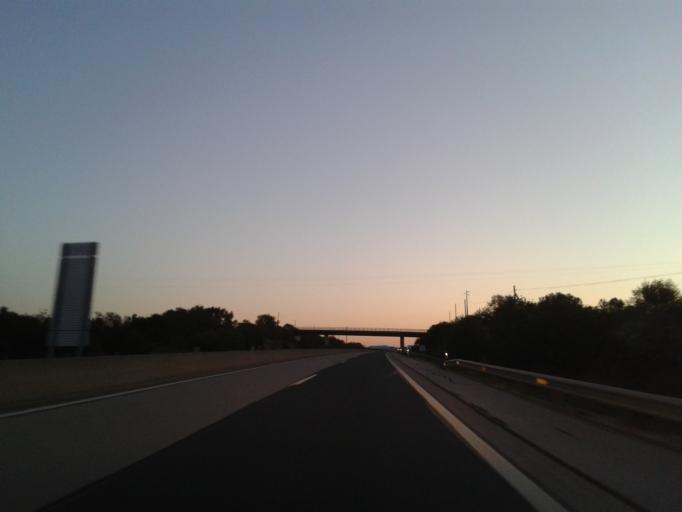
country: PT
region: Faro
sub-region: Albufeira
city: Ferreiras
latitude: 37.1406
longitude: -8.2290
